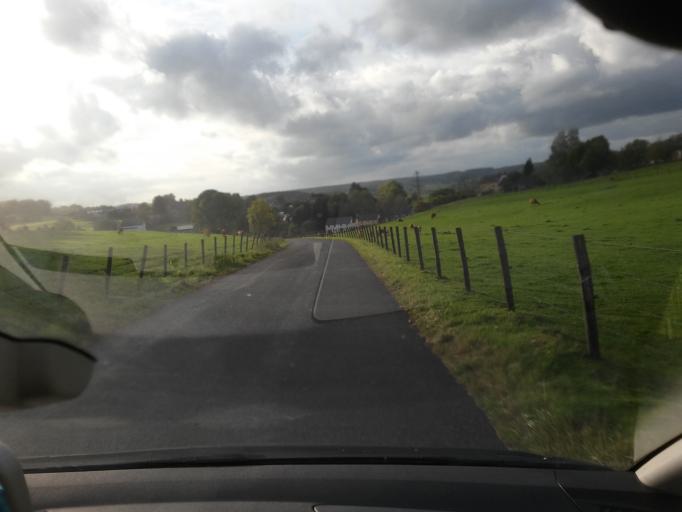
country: BE
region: Wallonia
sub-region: Province du Luxembourg
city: Attert
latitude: 49.7203
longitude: 5.7649
